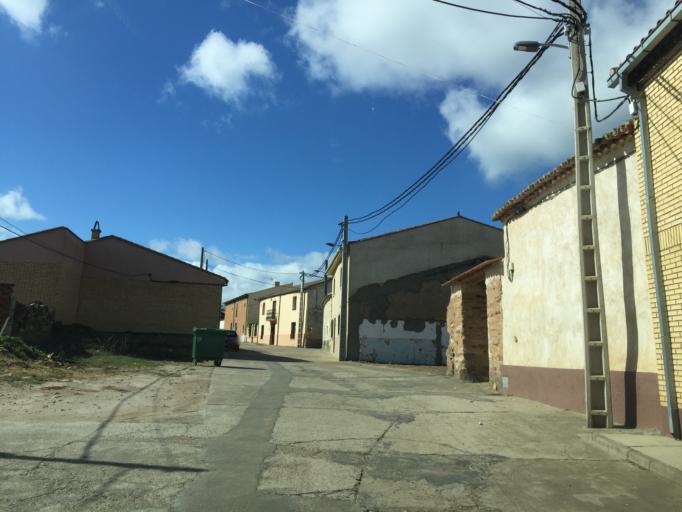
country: ES
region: Castille and Leon
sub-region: Provincia de Zamora
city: Montamarta
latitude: 41.6500
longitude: -5.8077
